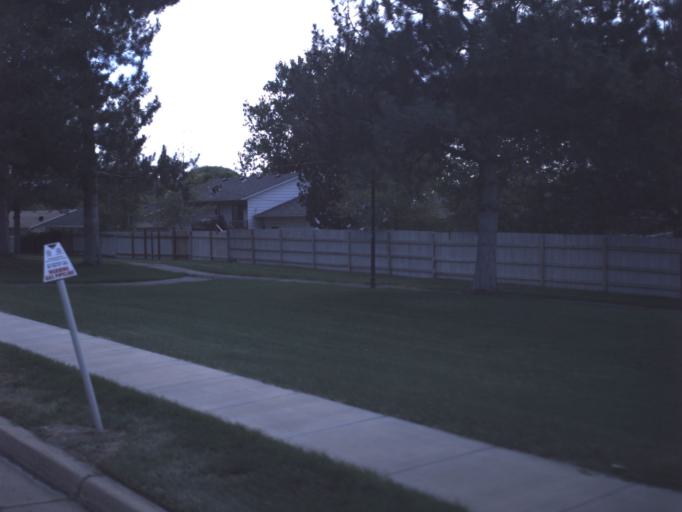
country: US
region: Utah
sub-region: Davis County
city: North Salt Lake
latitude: 40.8517
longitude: -111.9043
